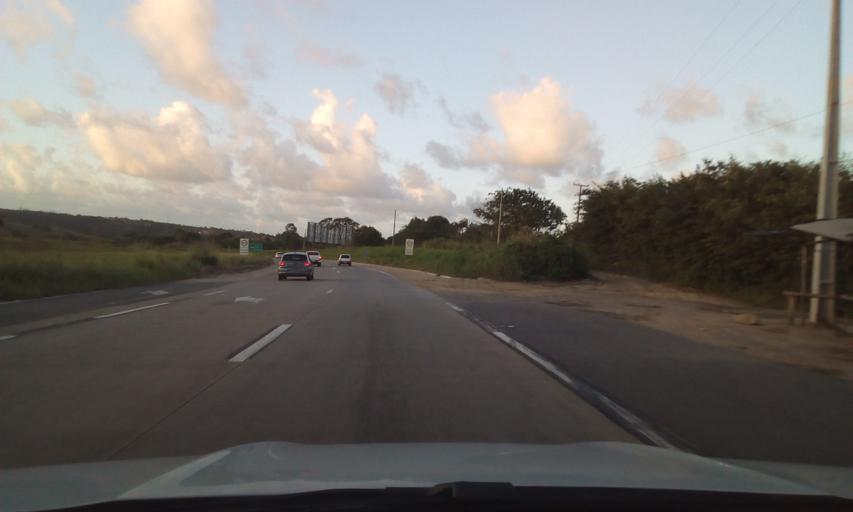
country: BR
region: Pernambuco
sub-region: Itapissuma
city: Itapissuma
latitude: -7.7018
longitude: -34.9226
